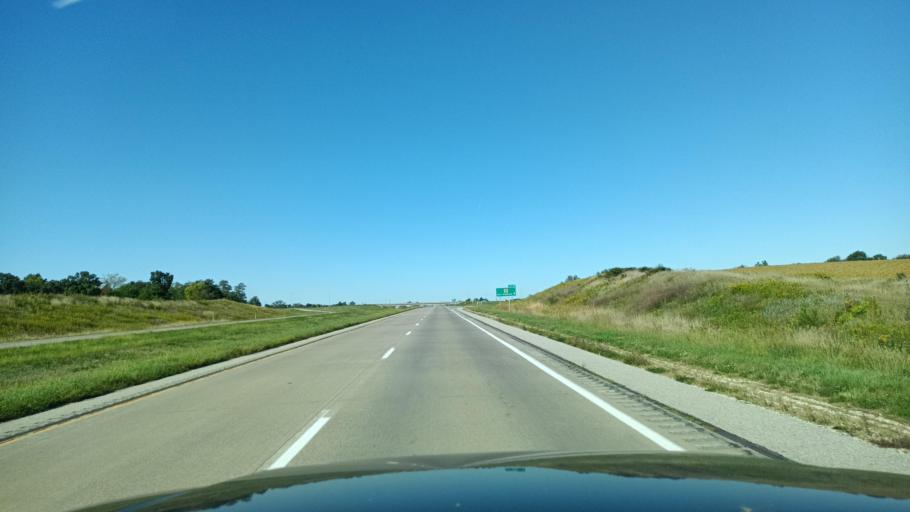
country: US
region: Iowa
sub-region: Lee County
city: Fort Madison
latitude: 40.6707
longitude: -91.3187
